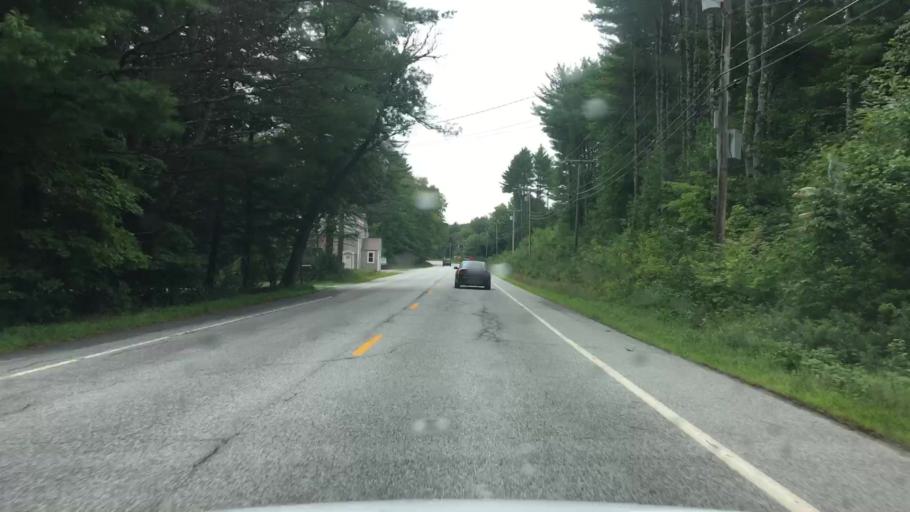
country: US
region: Maine
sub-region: York County
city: Cornish
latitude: 43.8237
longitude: -70.7735
